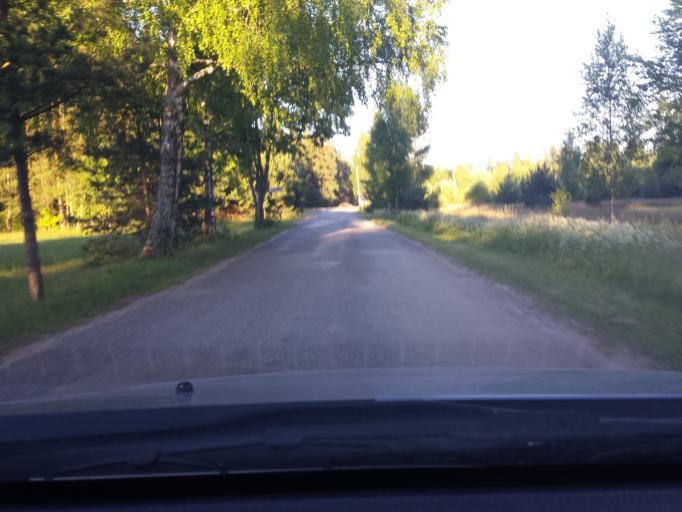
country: LV
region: Carnikava
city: Carnikava
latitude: 57.1151
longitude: 24.2399
